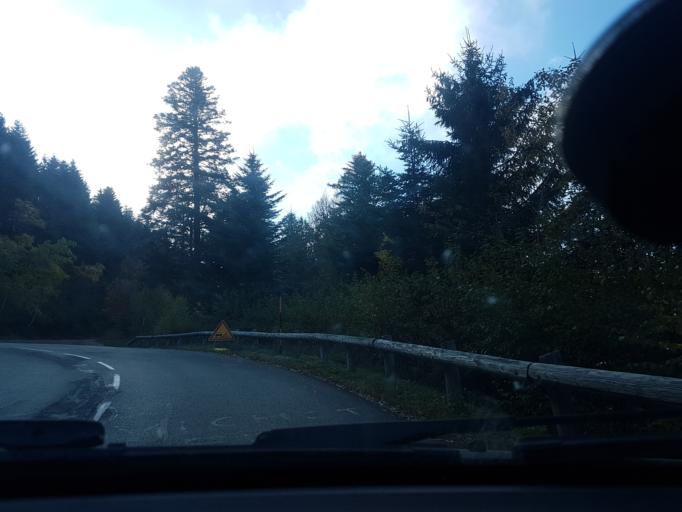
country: FR
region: Franche-Comte
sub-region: Departement de la Haute-Saone
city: Plancher-les-Mines
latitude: 47.7702
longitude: 6.7662
